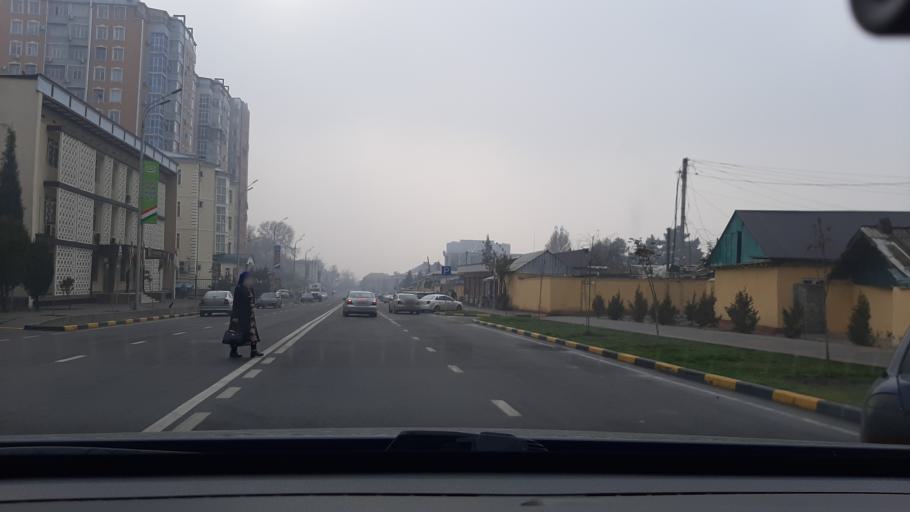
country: TJ
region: Dushanbe
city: Dushanbe
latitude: 38.5616
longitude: 68.7947
